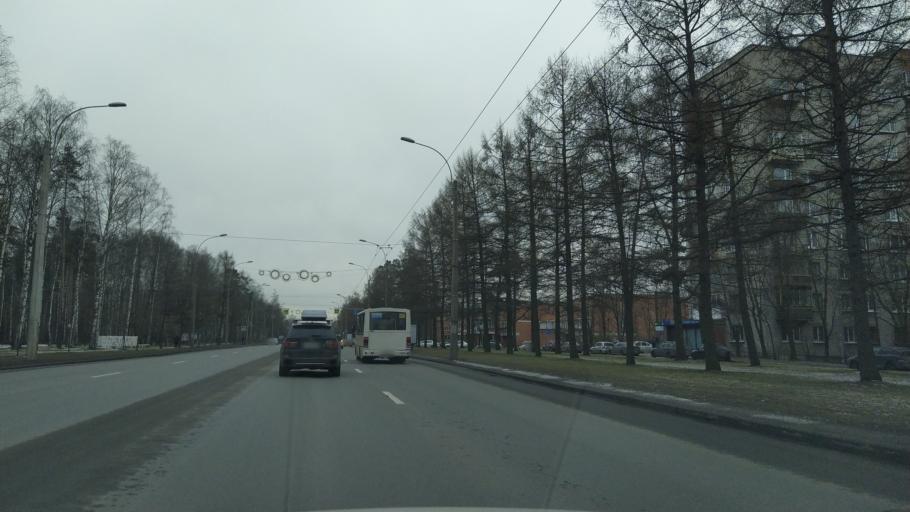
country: RU
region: St.-Petersburg
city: Sosnovka
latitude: 60.0157
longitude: 30.3391
